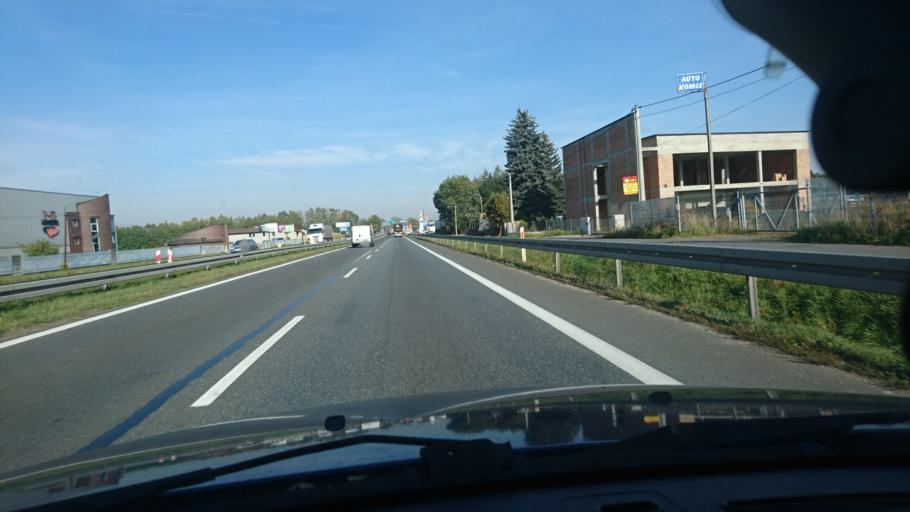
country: PL
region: Silesian Voivodeship
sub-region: Powiat pszczynski
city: Goczalkowice Zdroj
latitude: 49.9619
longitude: 18.9608
